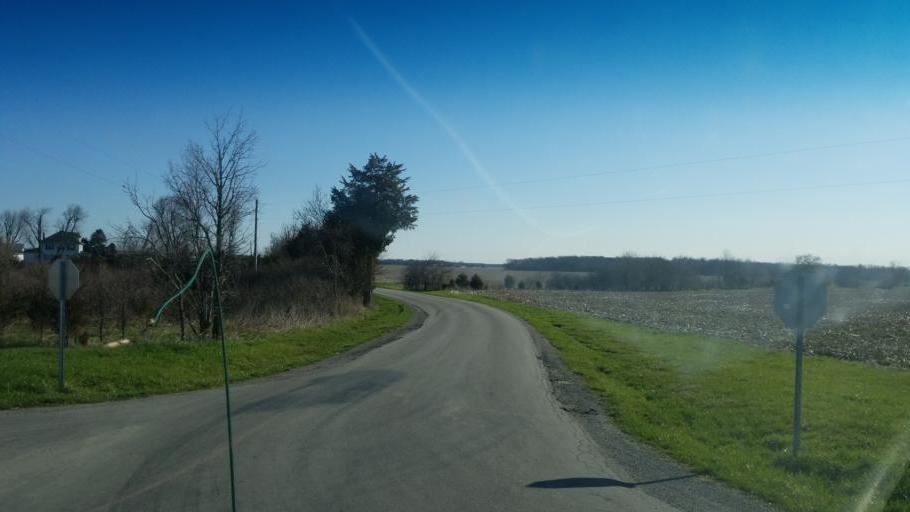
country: US
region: Ohio
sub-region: Logan County
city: Northwood
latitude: 40.5264
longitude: -83.6263
